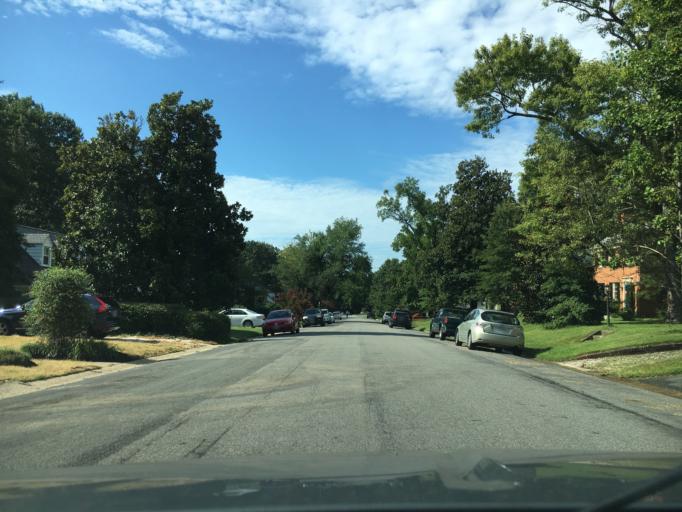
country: US
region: Virginia
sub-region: Henrico County
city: Tuckahoe
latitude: 37.5902
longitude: -77.5352
